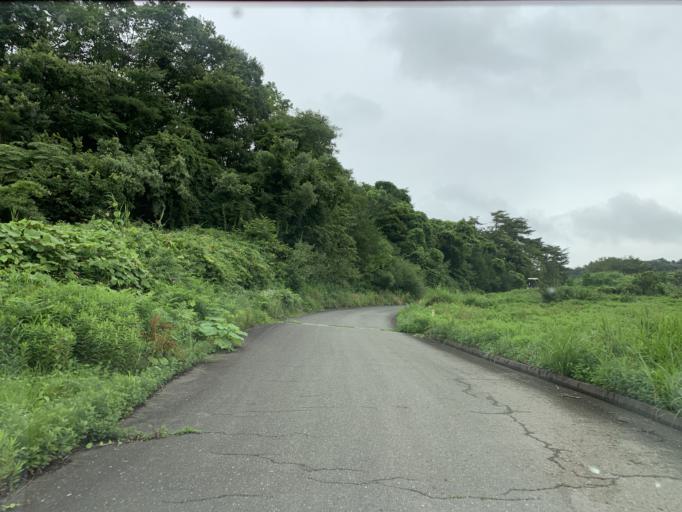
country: JP
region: Iwate
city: Ichinoseki
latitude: 38.8226
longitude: 141.2190
